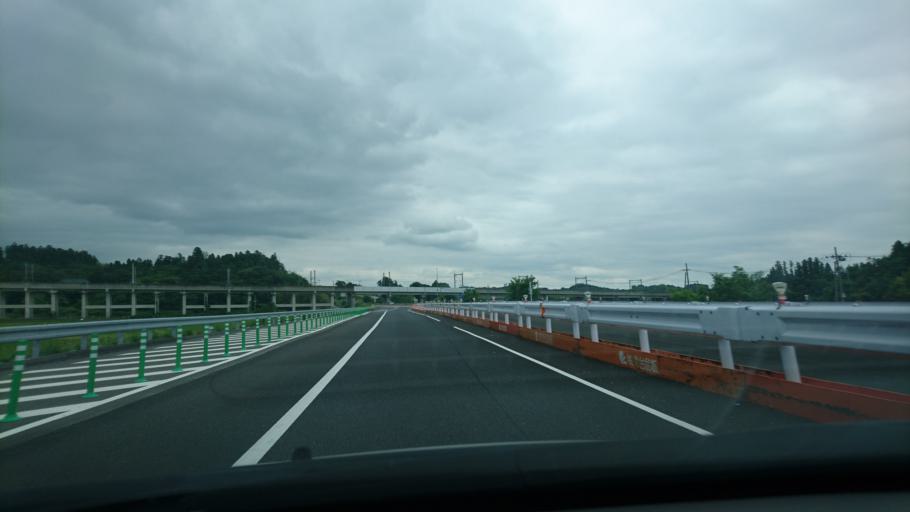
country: JP
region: Miyagi
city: Kogota
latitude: 38.7305
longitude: 141.0574
